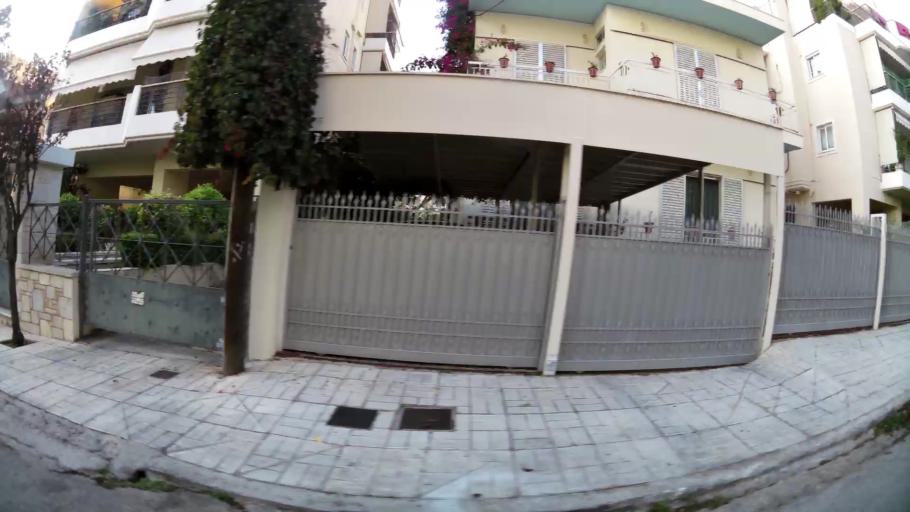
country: GR
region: Attica
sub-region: Nomarchia Athinas
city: Argyroupoli
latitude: 37.8991
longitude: 23.7718
